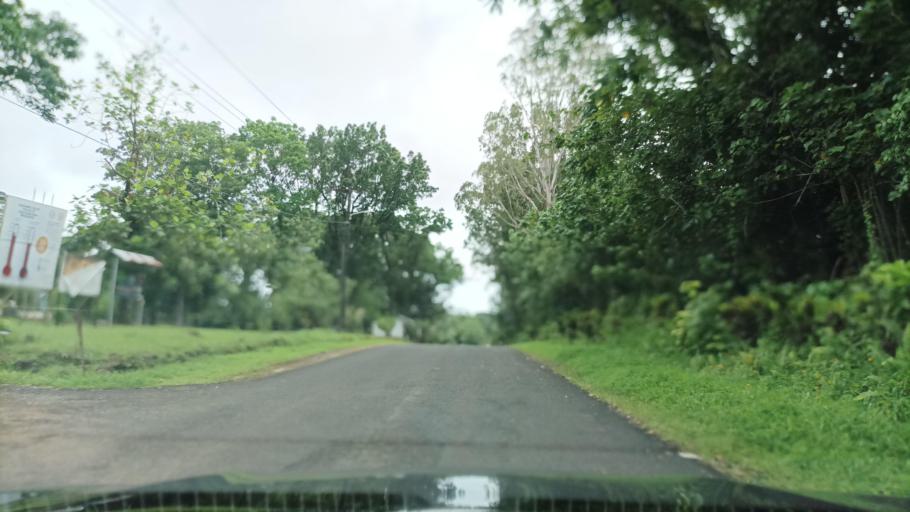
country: FM
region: Pohnpei
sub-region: Madolenihm Municipality
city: Madolenihm Municipality Government
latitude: 6.8355
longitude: 158.2983
